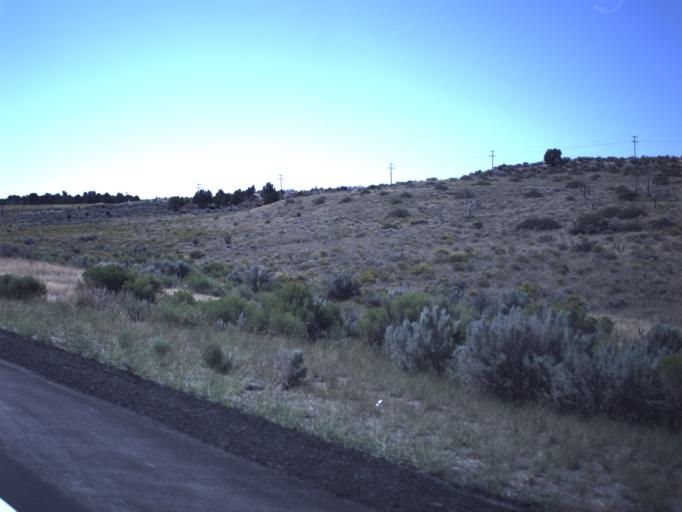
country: US
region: Utah
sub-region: Utah County
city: Genola
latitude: 39.9789
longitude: -112.2604
